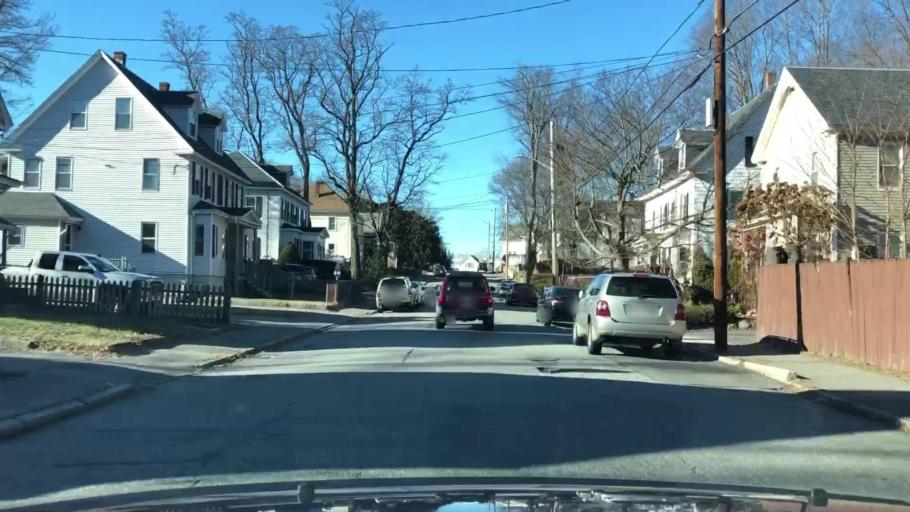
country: US
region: Massachusetts
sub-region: Middlesex County
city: Dracut
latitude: 42.6622
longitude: -71.3060
